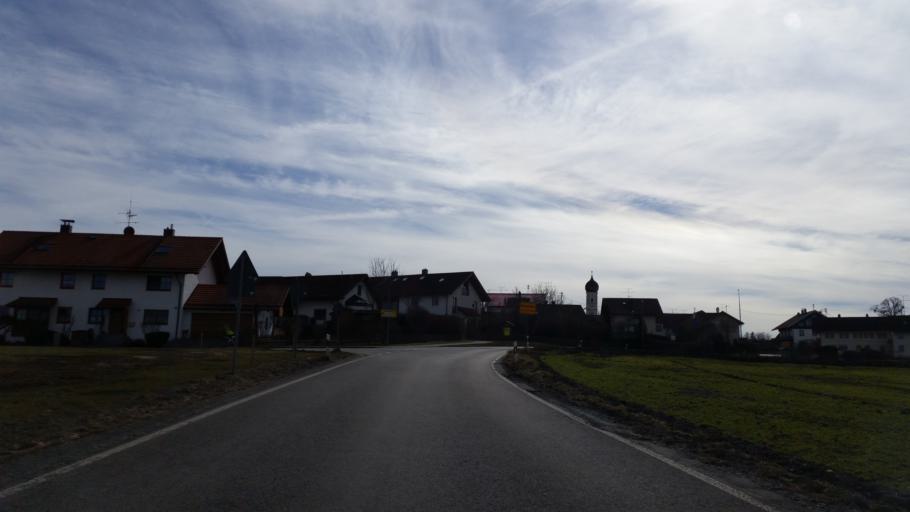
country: DE
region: Bavaria
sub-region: Upper Bavaria
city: Oberpframmern
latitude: 48.0250
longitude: 11.8141
